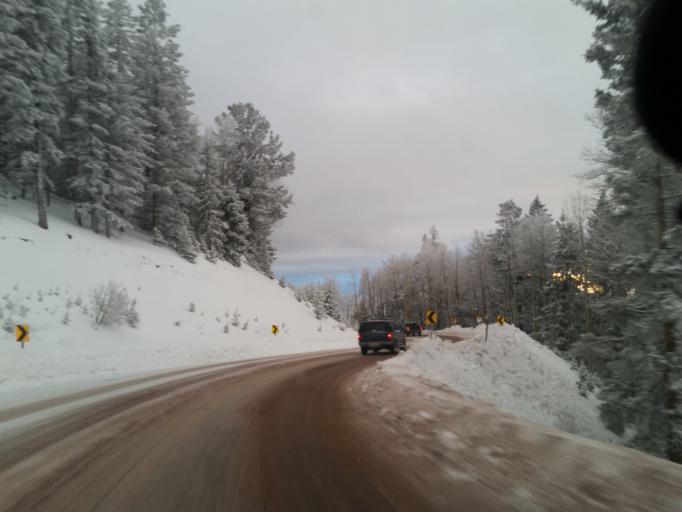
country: US
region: New Mexico
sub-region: Santa Fe County
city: Santa Fe
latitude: 35.7824
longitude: -105.8081
